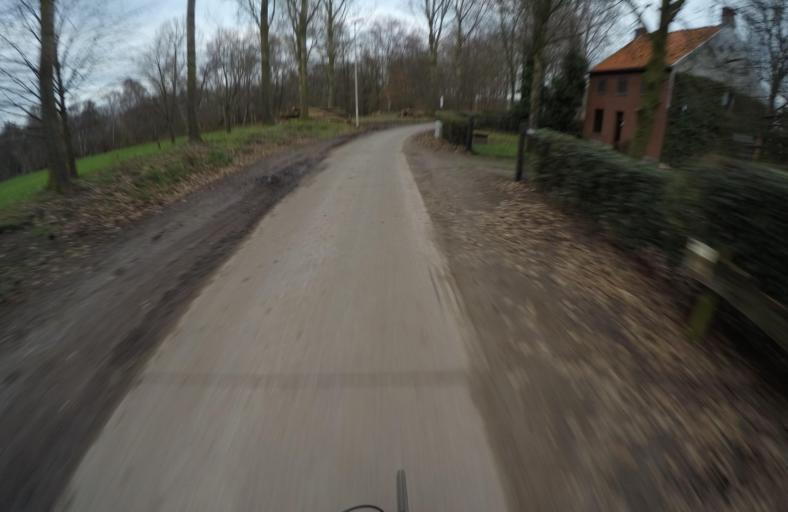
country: BE
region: Flanders
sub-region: Provincie Oost-Vlaanderen
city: Sint-Gillis-Waas
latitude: 51.2414
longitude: 4.1332
